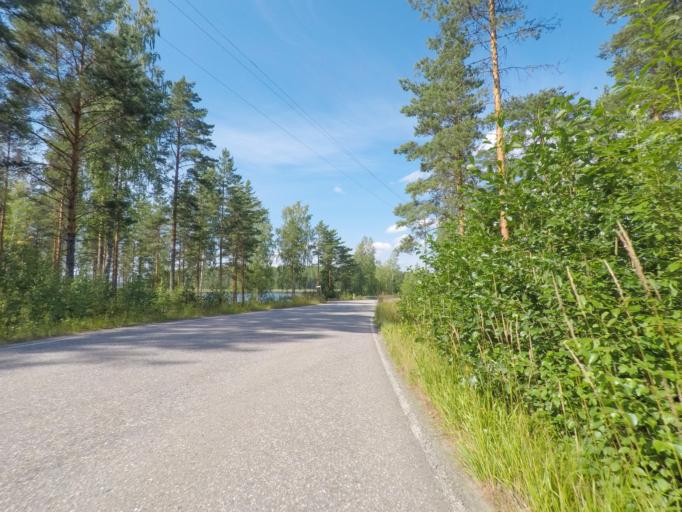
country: FI
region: Southern Savonia
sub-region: Mikkeli
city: Puumala
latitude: 61.4707
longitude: 28.1671
